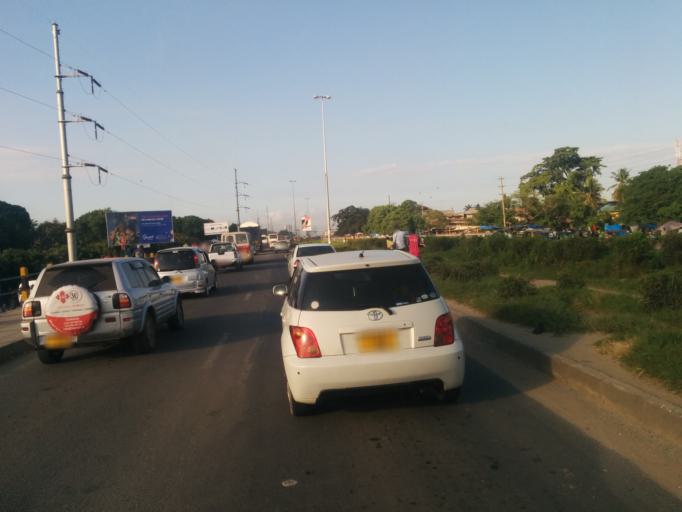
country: TZ
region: Dar es Salaam
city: Magomeni
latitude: -6.7893
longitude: 39.2088
